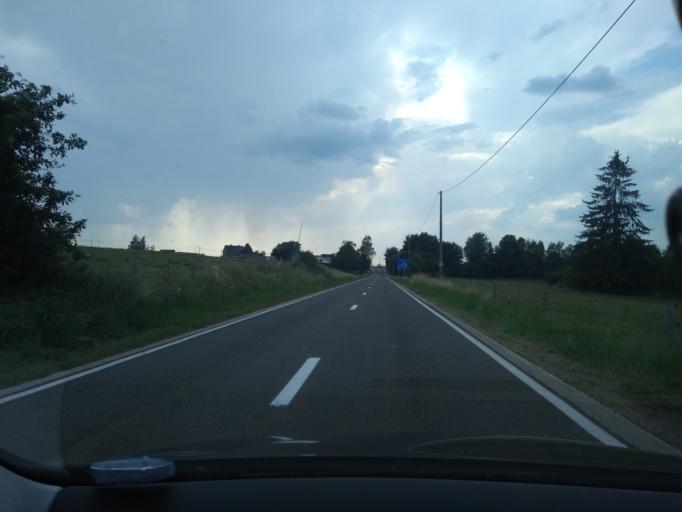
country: BE
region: Wallonia
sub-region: Province du Luxembourg
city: Bertogne
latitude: 50.0805
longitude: 5.6700
